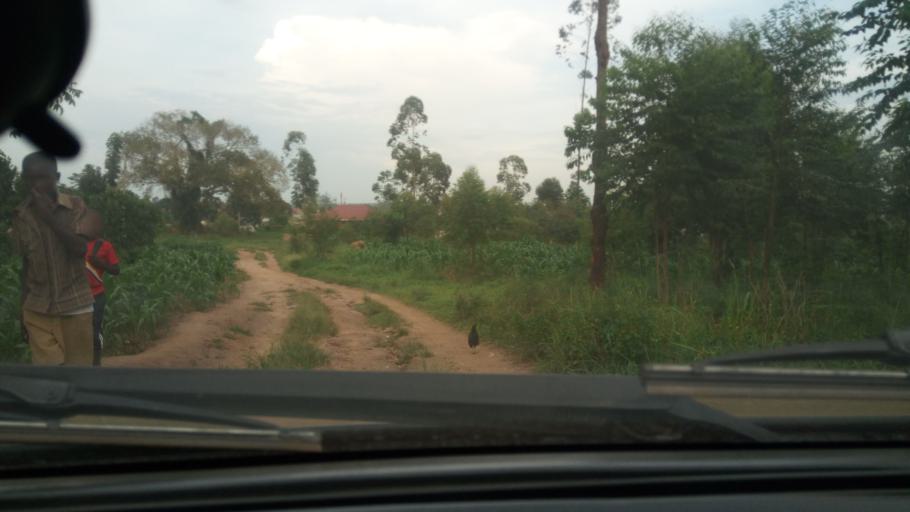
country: UG
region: Central Region
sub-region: Mityana District
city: Mityana
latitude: 0.5661
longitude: 32.1984
